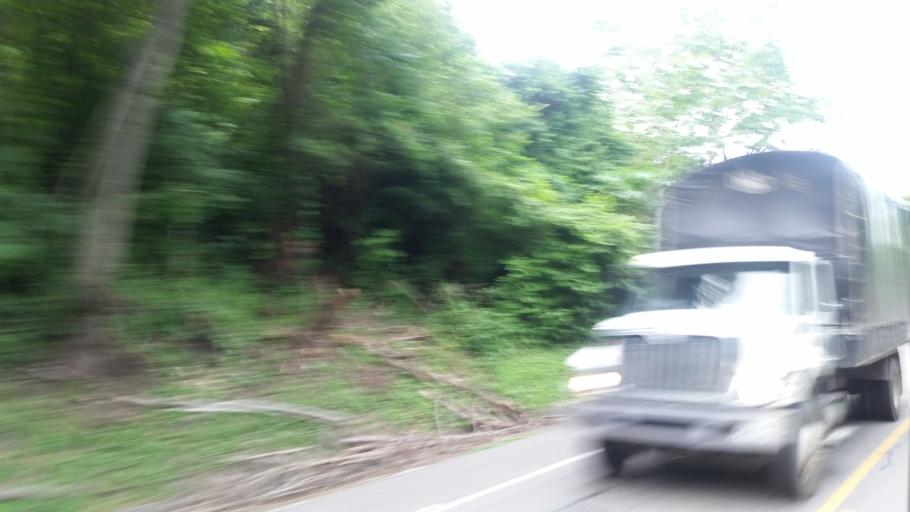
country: CO
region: Magdalena
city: Santa Marta
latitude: 11.2887
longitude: -73.8876
